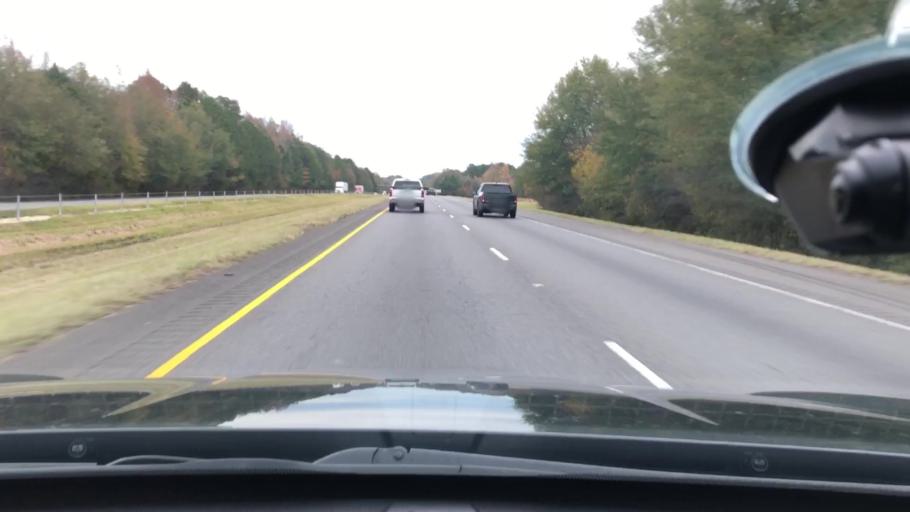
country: US
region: Arkansas
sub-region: Clark County
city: Gurdon
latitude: 34.0171
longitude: -93.1630
